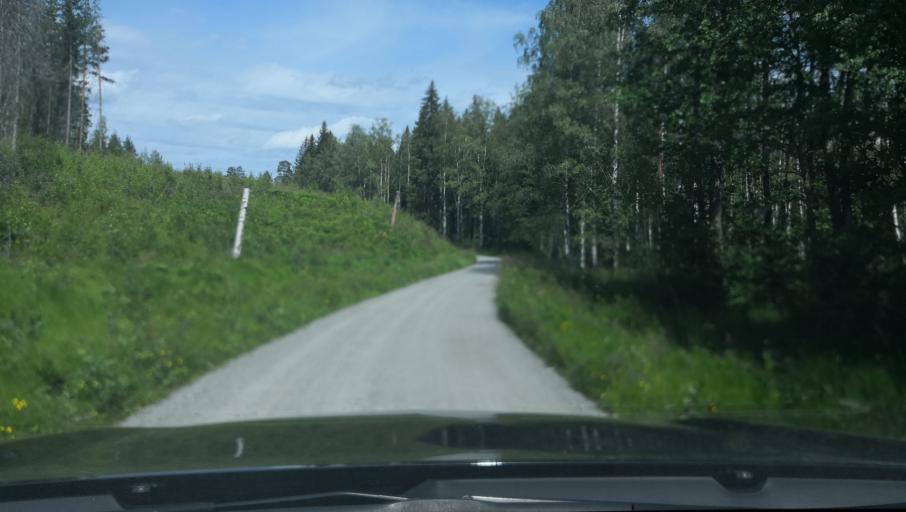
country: SE
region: Vaestmanland
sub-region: Surahammars Kommun
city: Ramnas
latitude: 59.8891
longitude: 16.0980
